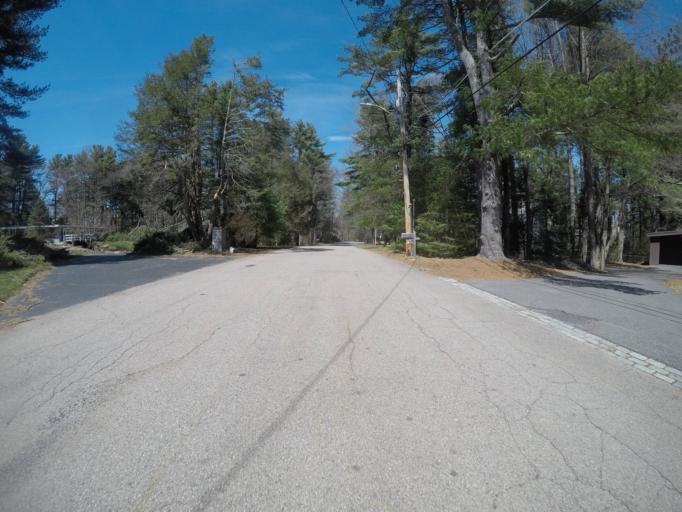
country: US
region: Massachusetts
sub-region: Bristol County
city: Easton
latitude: 42.0470
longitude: -71.0905
